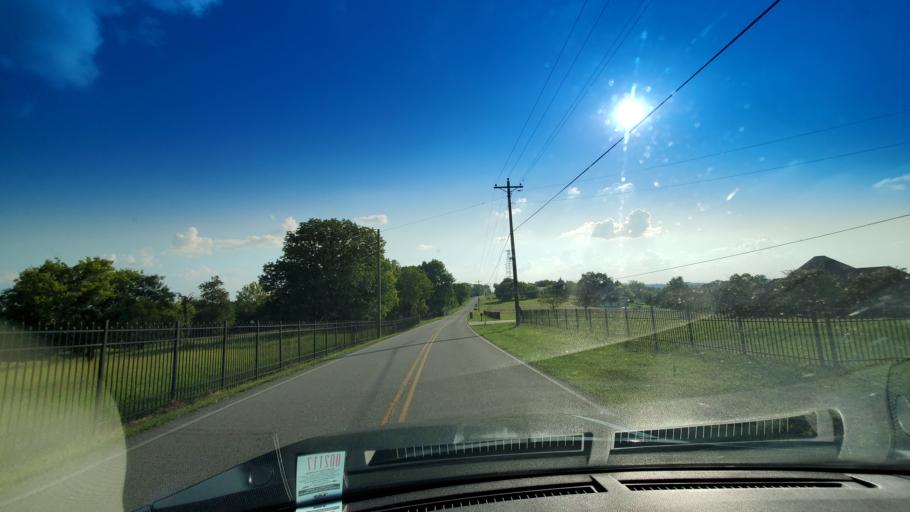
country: US
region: Tennessee
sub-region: Wilson County
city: Rural Hill
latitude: 36.1525
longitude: -86.3805
